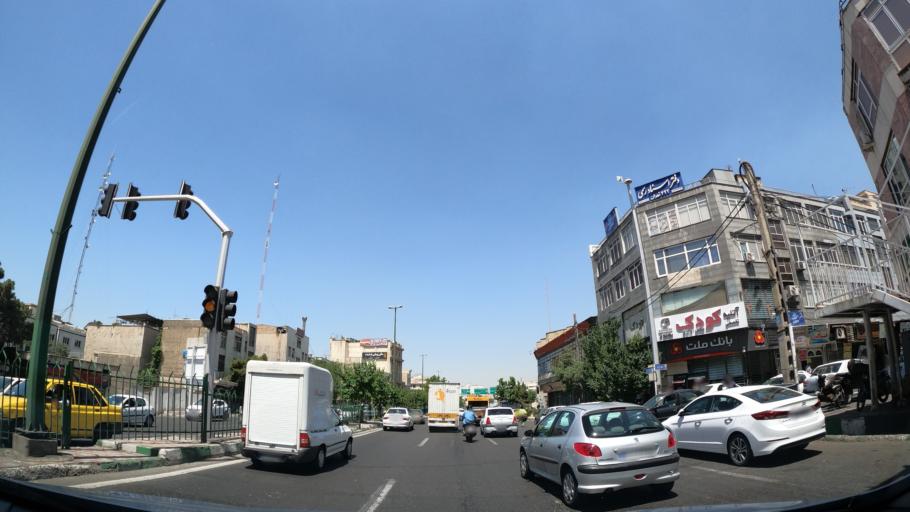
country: IR
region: Tehran
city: Tehran
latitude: 35.7272
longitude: 51.3737
